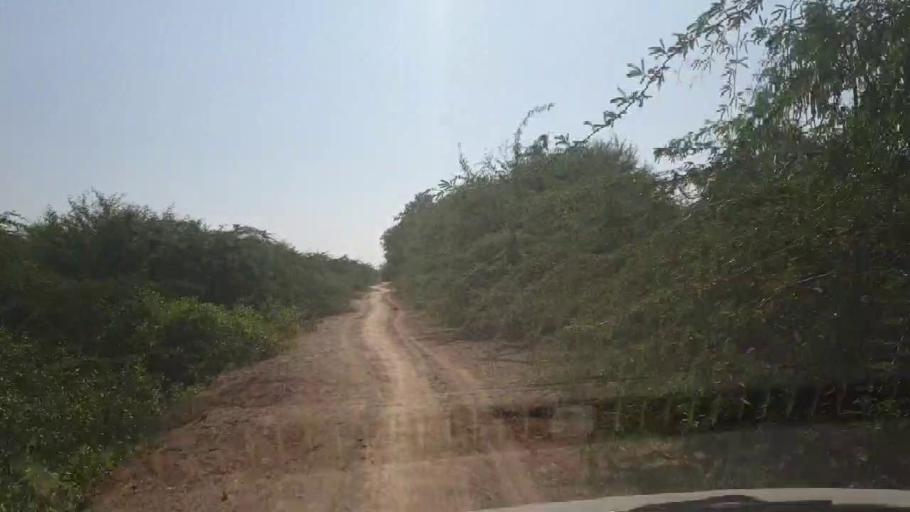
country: PK
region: Sindh
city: Tando Bago
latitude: 24.8995
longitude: 69.1645
